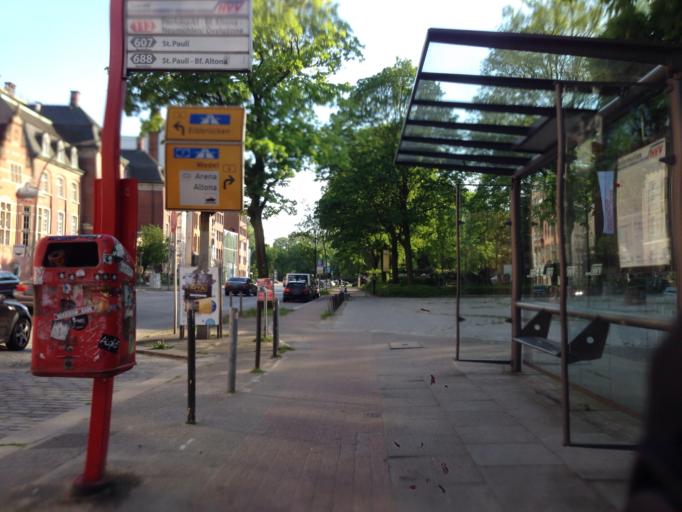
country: DE
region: Hamburg
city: Neustadt
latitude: 53.5515
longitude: 9.9747
